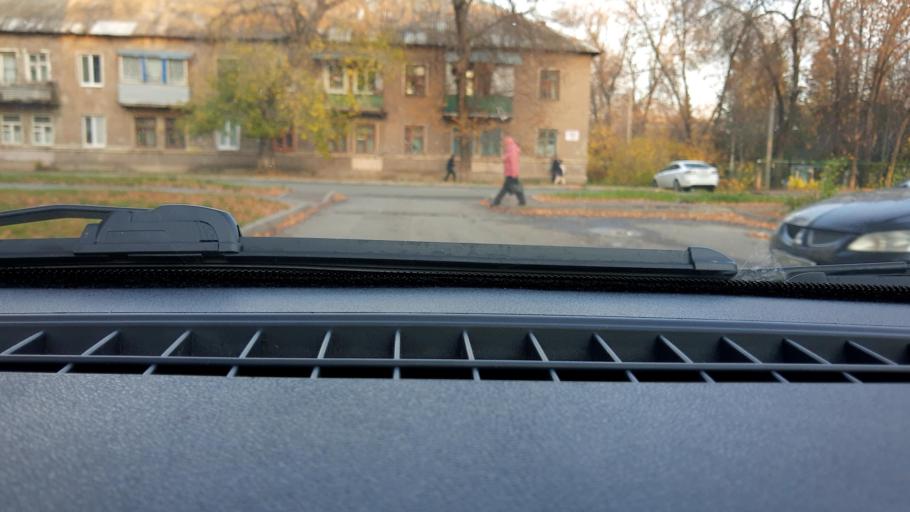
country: RU
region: Bashkortostan
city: Ufa
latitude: 54.8136
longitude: 56.1185
